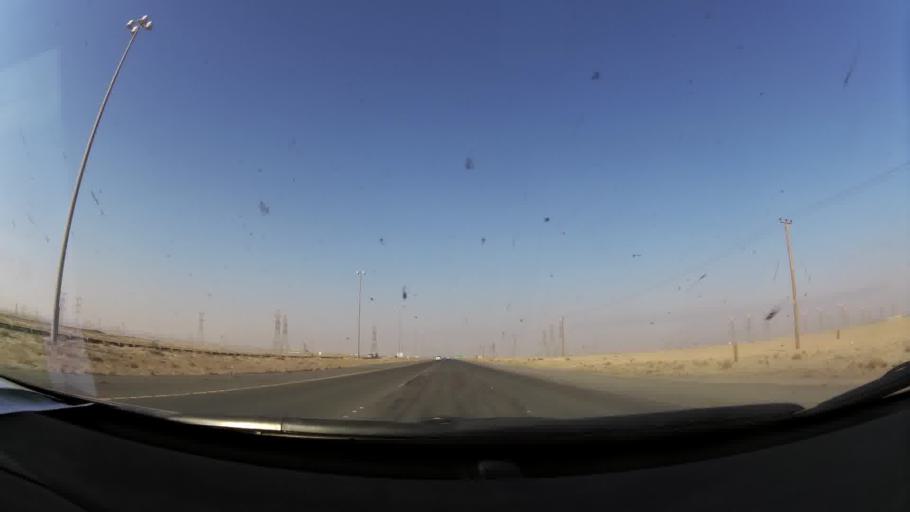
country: IQ
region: Basra Governorate
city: Umm Qasr
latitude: 29.8227
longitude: 47.6757
